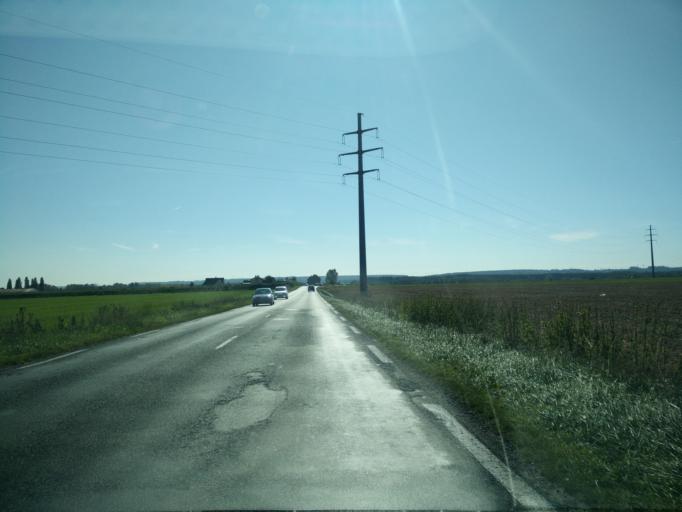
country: FR
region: Ile-de-France
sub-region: Departement de Seine-et-Marne
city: Claye-Souilly
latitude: 48.9730
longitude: 2.6613
